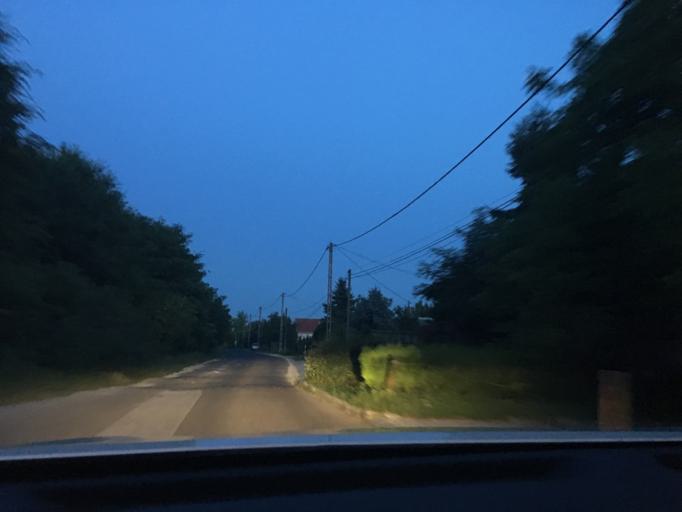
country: HU
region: Budapest
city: Budapest XVII. keruelet
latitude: 47.4694
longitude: 19.2733
